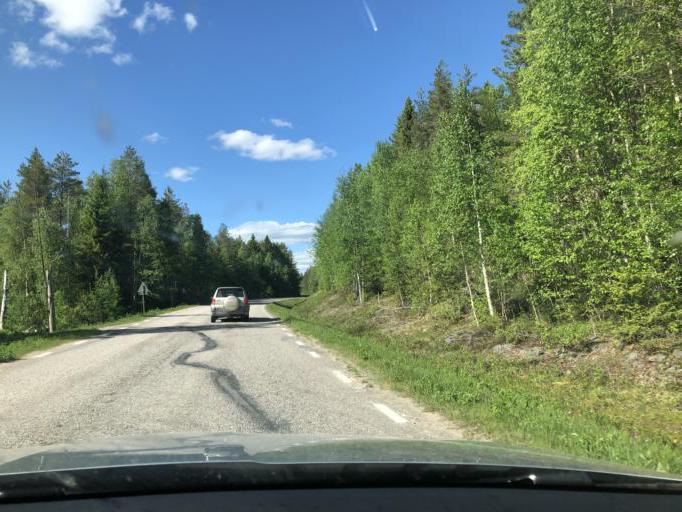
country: SE
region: Norrbotten
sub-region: Kalix Kommun
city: Kalix
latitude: 66.0005
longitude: 23.1425
